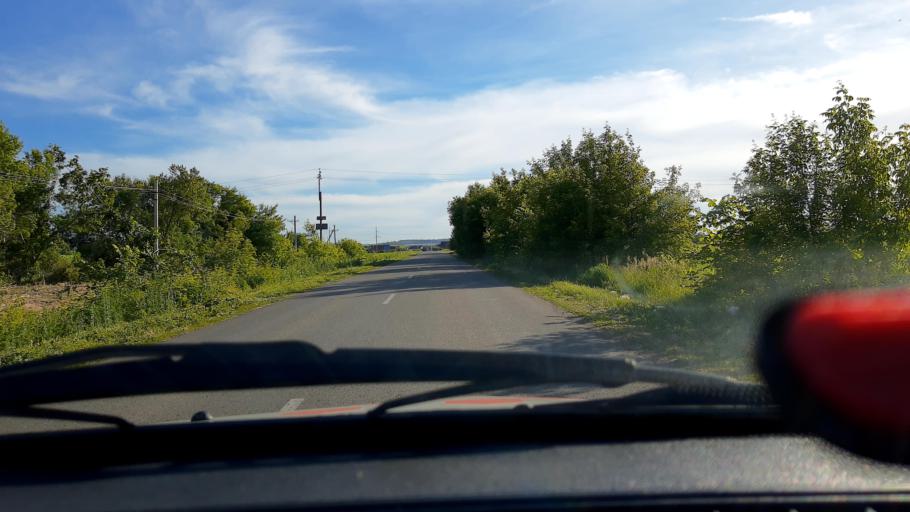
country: RU
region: Bashkortostan
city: Kabakovo
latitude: 54.5081
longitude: 55.9330
